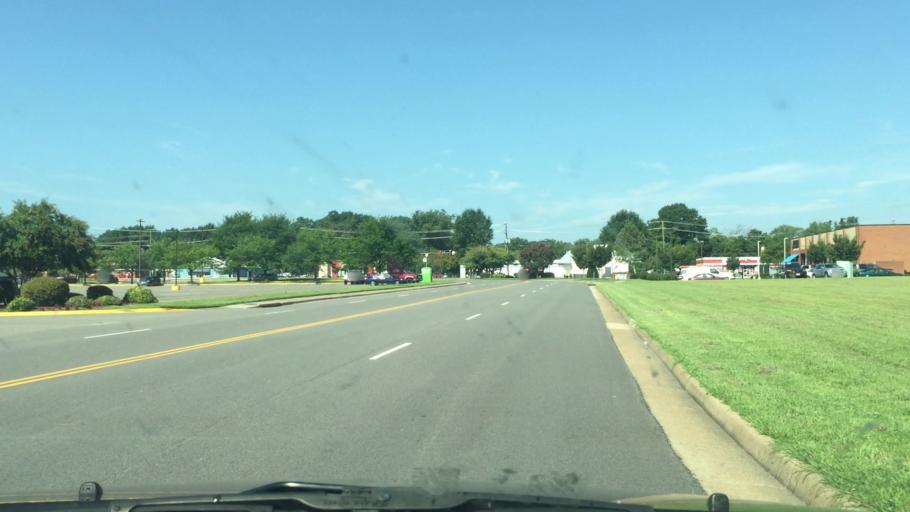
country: US
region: Virginia
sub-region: Hanover County
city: Ashland
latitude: 37.7559
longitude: -77.4688
